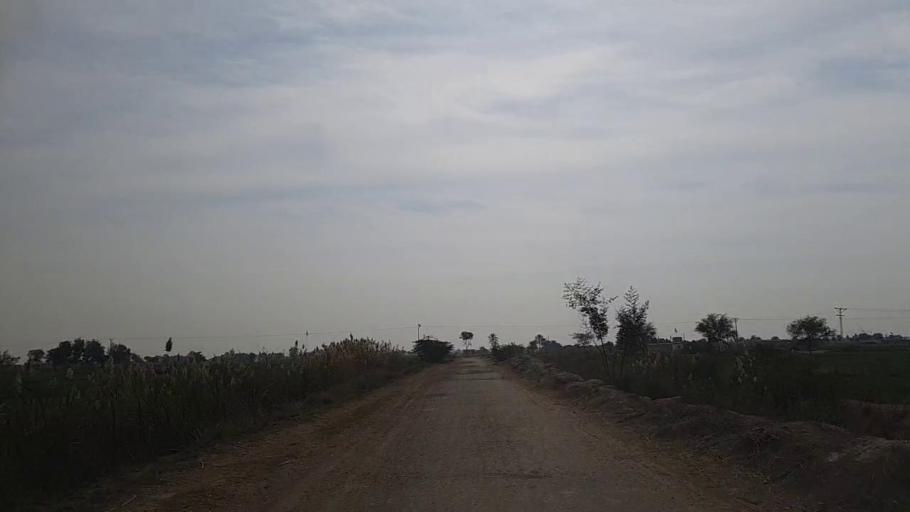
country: PK
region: Sindh
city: Daur
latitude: 26.4529
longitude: 68.4353
